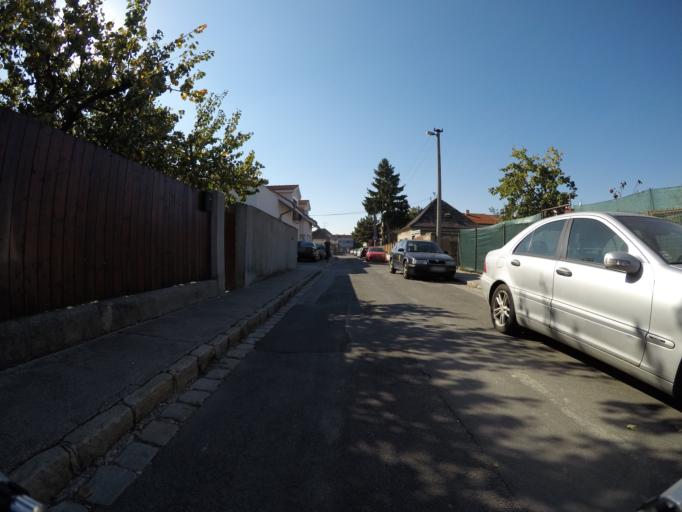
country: SK
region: Bratislavsky
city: Bratislava
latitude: 48.1717
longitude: 17.1659
